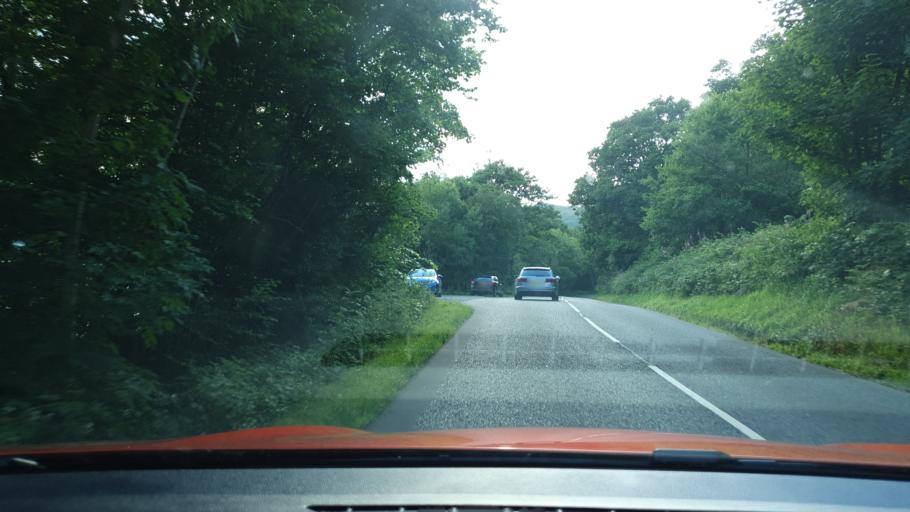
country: GB
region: England
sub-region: Cumbria
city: Ambleside
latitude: 54.5747
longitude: -2.9105
